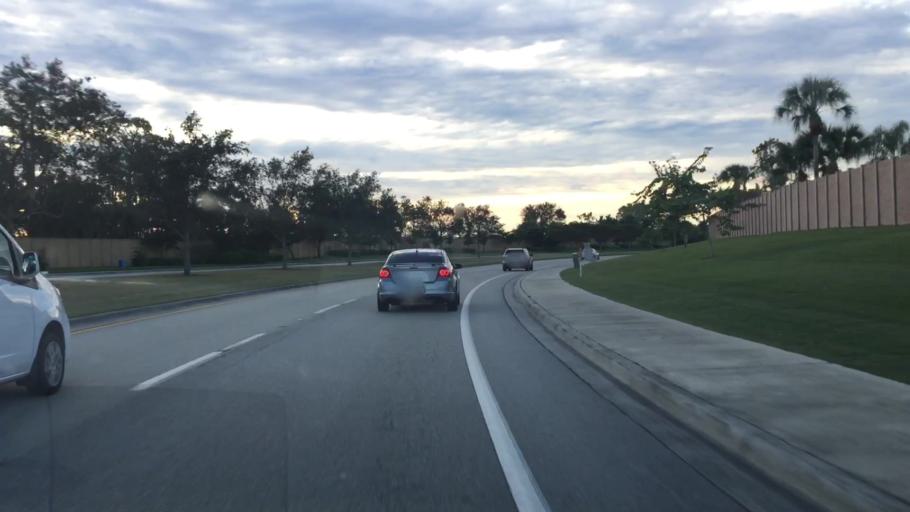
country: US
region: Florida
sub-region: Lee County
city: Gateway
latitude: 26.5933
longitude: -81.7844
